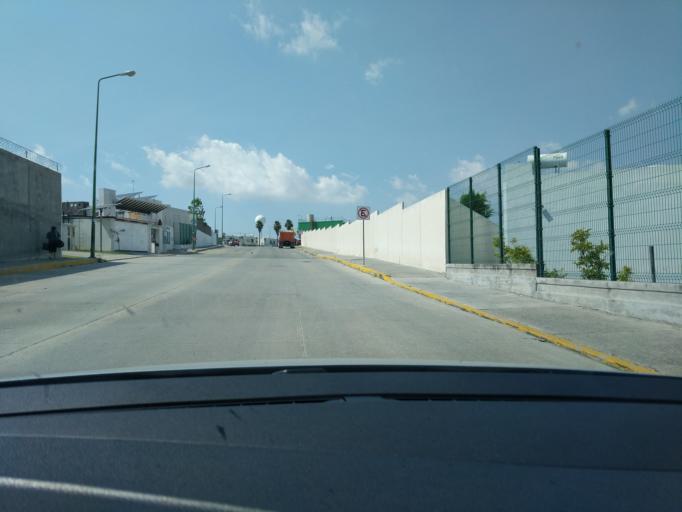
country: MX
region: Puebla
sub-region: Puebla
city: Galaxia la Calera
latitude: 19.0044
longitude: -98.1472
